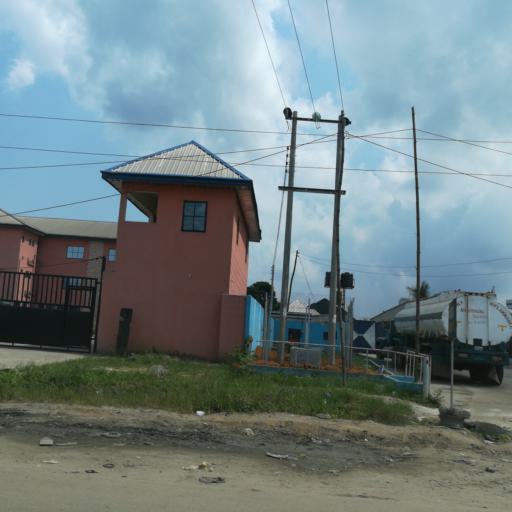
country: NG
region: Rivers
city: Okrika
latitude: 4.8146
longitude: 7.0964
